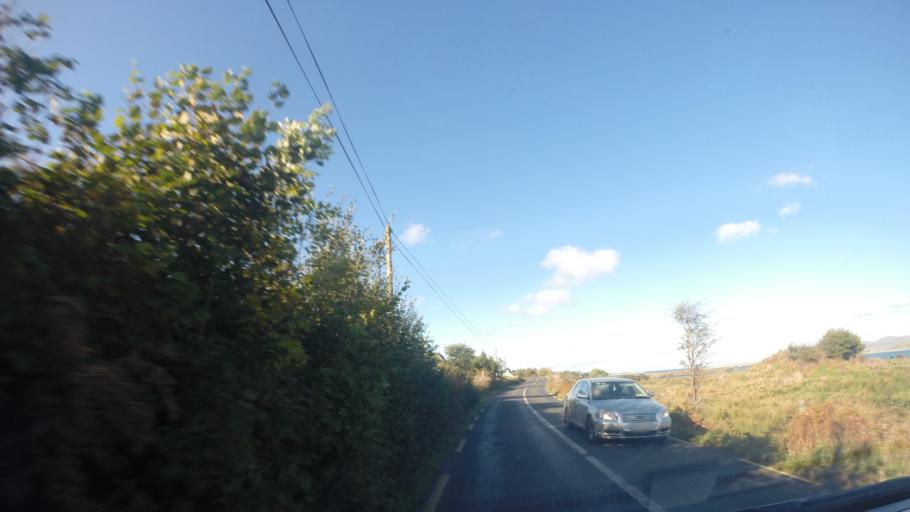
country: IE
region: Ulster
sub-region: County Donegal
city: Dungloe
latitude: 54.8337
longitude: -8.3488
